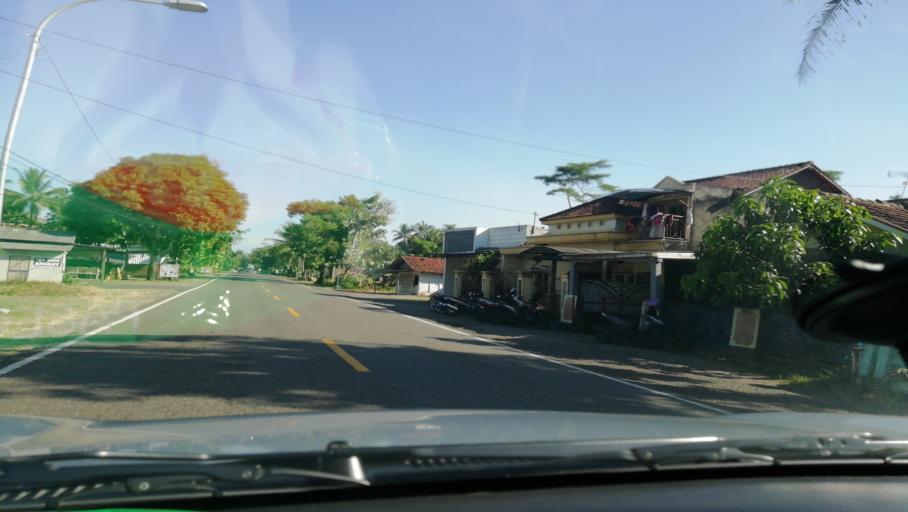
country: ID
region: Central Java
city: Kutoarjo
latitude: -7.7426
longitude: 109.9996
